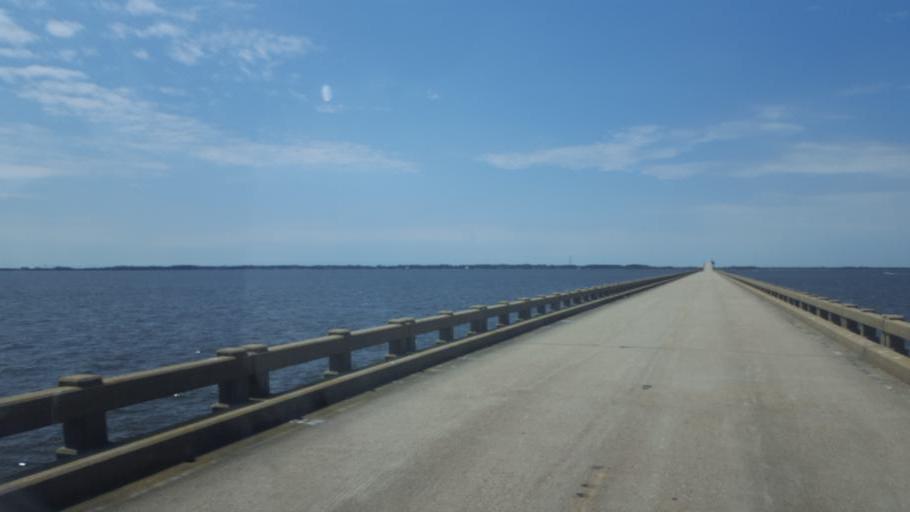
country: US
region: North Carolina
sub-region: Dare County
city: Manteo
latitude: 35.9225
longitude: -75.7376
